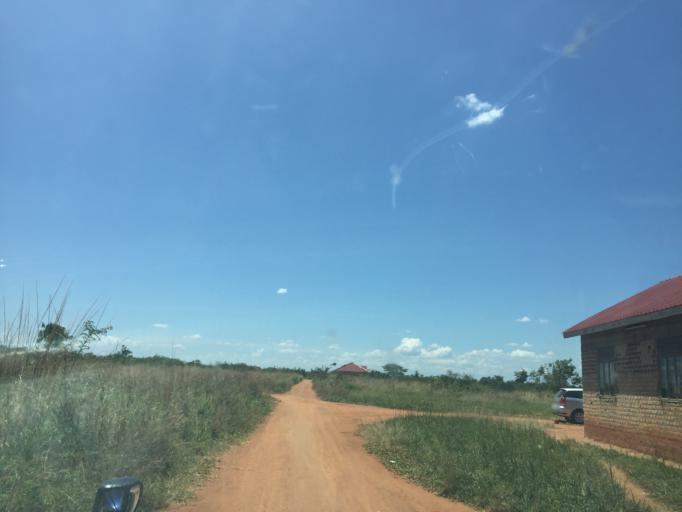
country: UG
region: Western Region
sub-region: Kiryandongo District
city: Masindi Port
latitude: 1.5060
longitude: 32.0990
